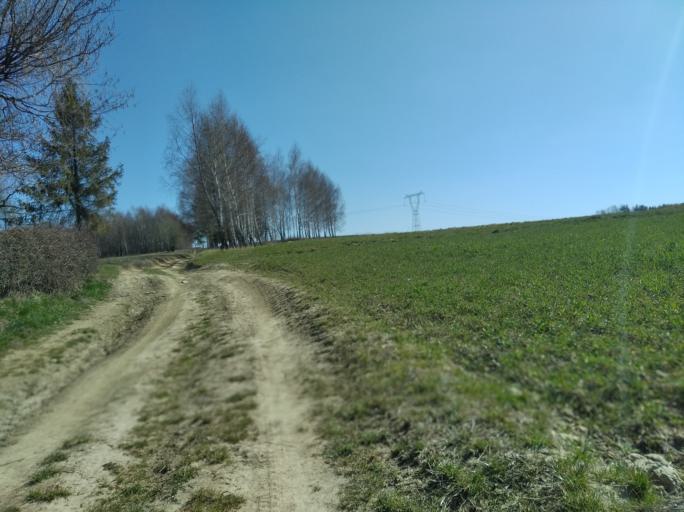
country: PL
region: Subcarpathian Voivodeship
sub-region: Powiat strzyzowski
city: Polomia
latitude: 49.8833
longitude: 21.8468
